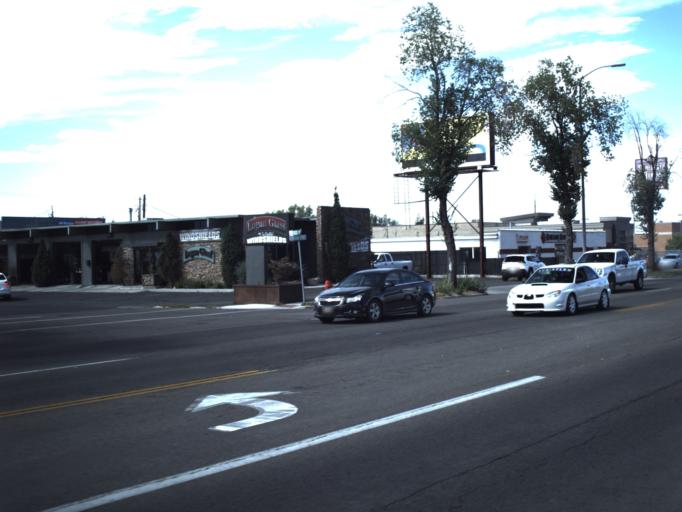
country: US
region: Utah
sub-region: Cache County
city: Logan
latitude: 41.7481
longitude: -111.8345
